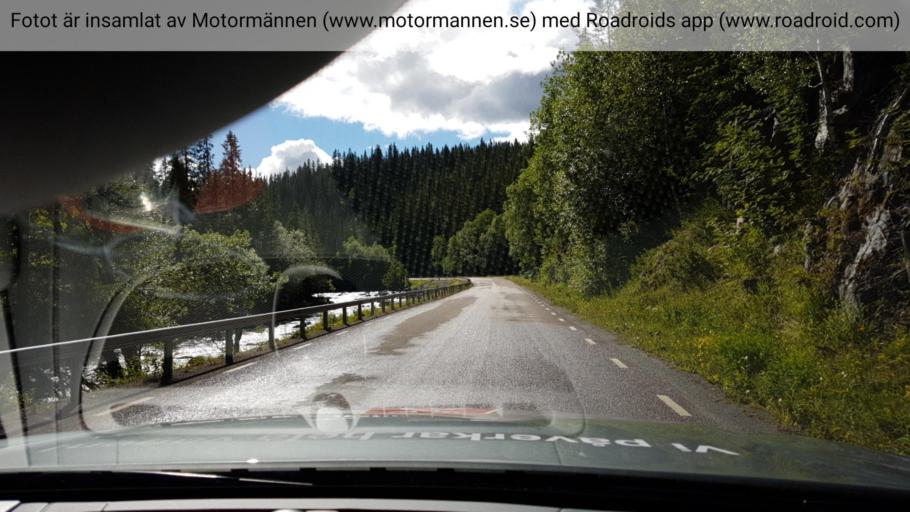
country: SE
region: Jaemtland
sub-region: Are Kommun
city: Jarpen
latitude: 63.1067
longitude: 13.8538
